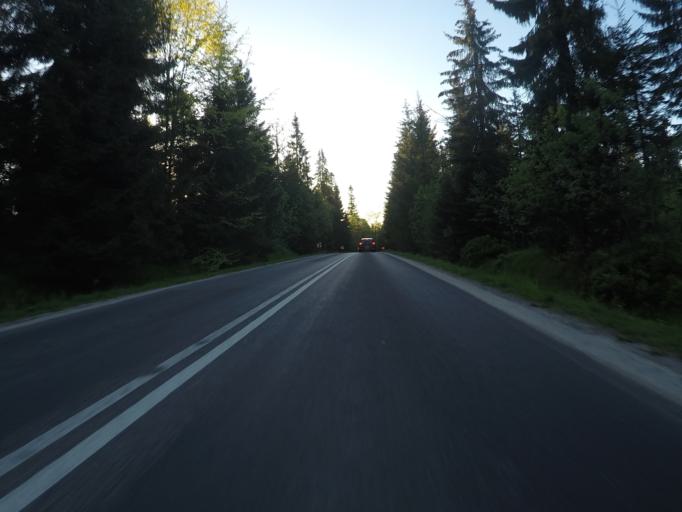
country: PL
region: Lesser Poland Voivodeship
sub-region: Powiat tatrzanski
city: Bukowina Tatrzanska
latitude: 49.2894
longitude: 20.1040
